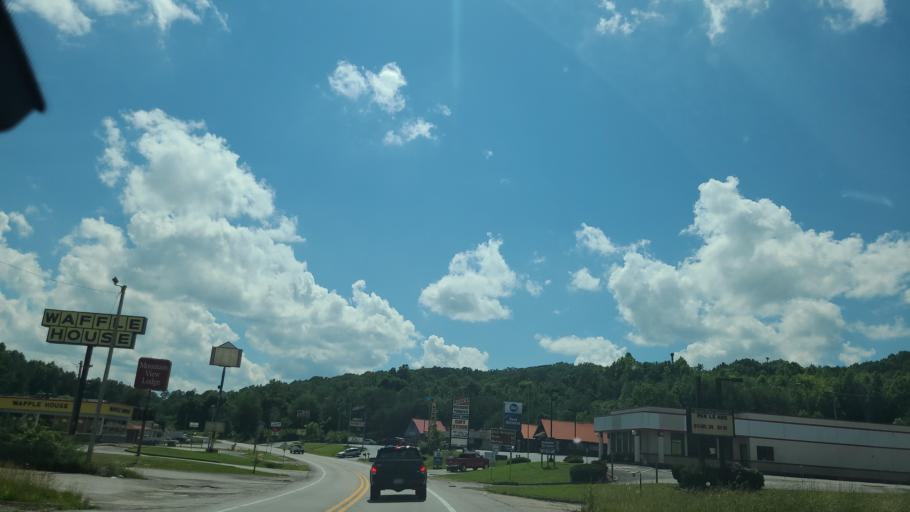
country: US
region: Kentucky
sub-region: Whitley County
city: Corbin
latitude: 36.9179
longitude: -84.1323
